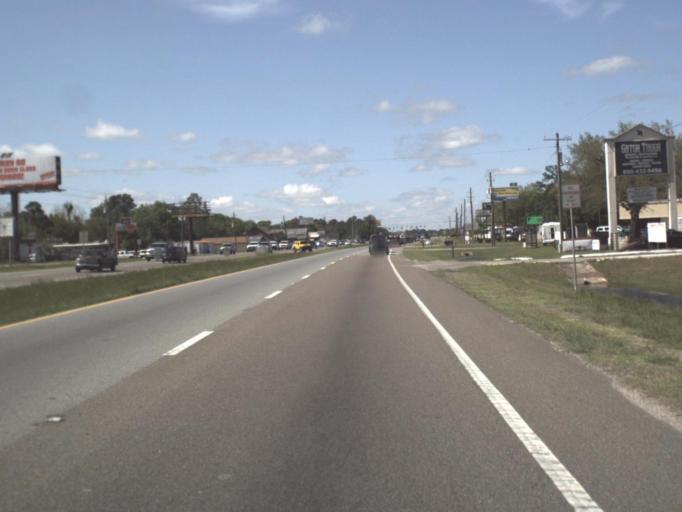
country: US
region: Florida
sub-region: Escambia County
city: Ensley
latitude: 30.5143
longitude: -87.2713
